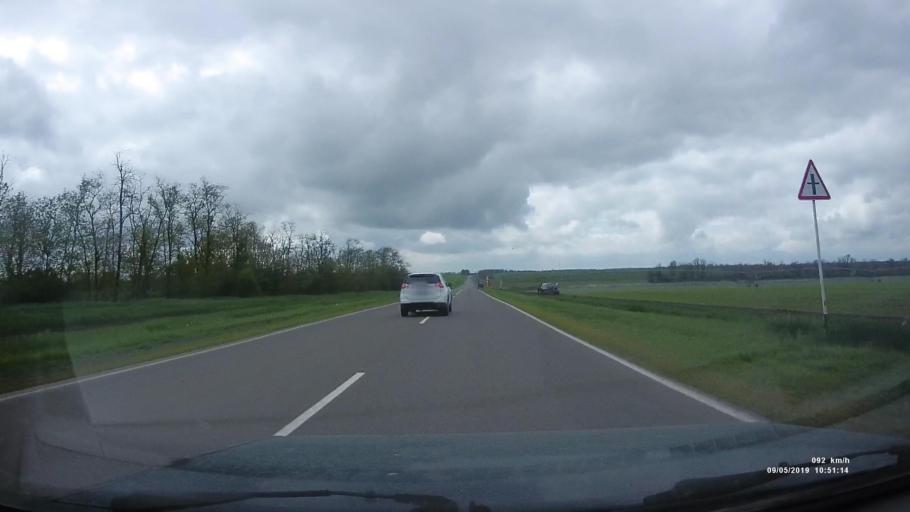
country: RU
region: Rostov
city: Peshkovo
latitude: 46.9175
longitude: 39.3552
